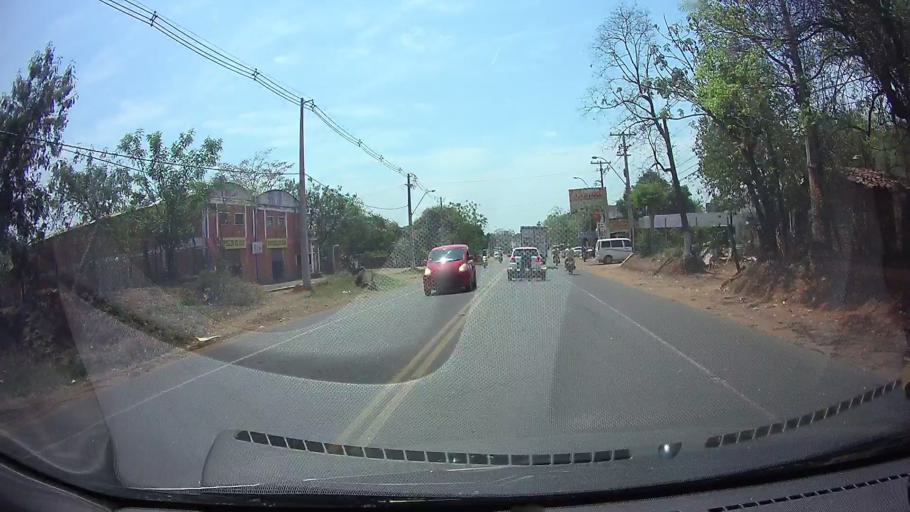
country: PY
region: Central
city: Capiata
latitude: -25.4008
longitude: -57.4645
